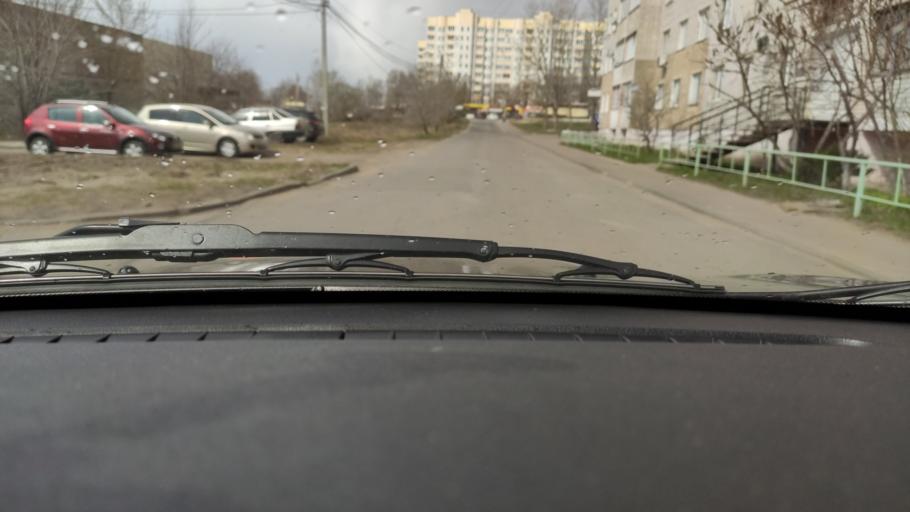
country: RU
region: Voronezj
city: Shilovo
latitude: 51.5595
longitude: 39.1131
